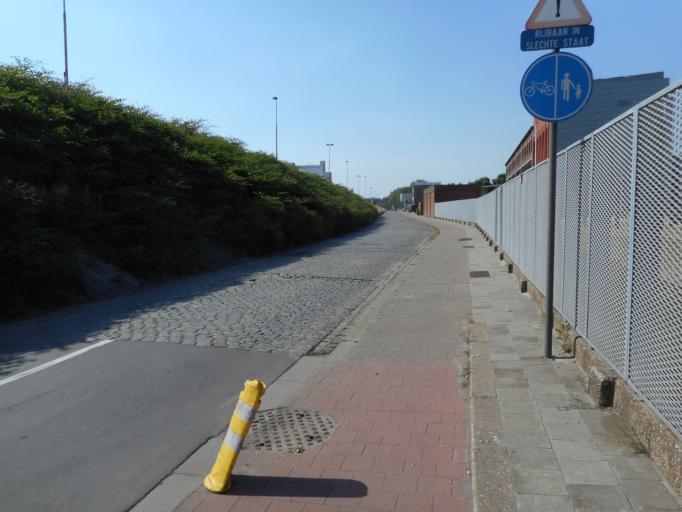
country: BE
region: Flanders
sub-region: Provincie Antwerpen
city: Schoten
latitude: 51.2381
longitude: 4.4543
